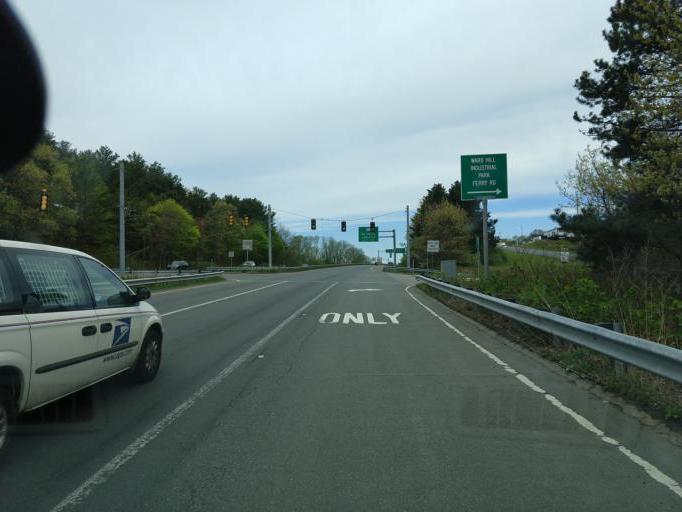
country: US
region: Massachusetts
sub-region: Essex County
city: Haverhill
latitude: 42.7518
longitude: -71.1101
